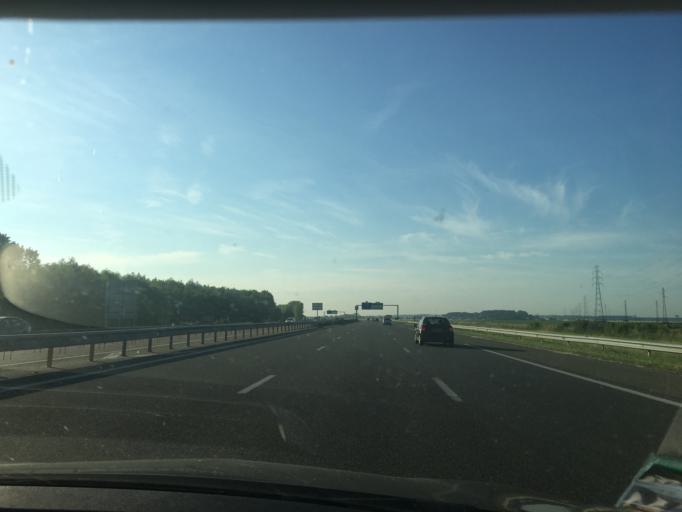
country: FR
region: Ile-de-France
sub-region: Departement de Seine-et-Marne
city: Moissy-Cramayel
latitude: 48.5975
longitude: 2.6086
